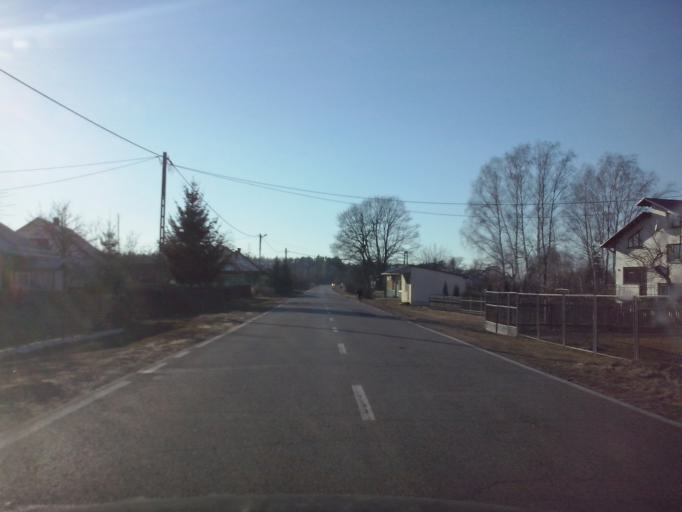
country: PL
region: Subcarpathian Voivodeship
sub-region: Powiat nizanski
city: Harasiuki
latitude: 50.5178
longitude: 22.4732
